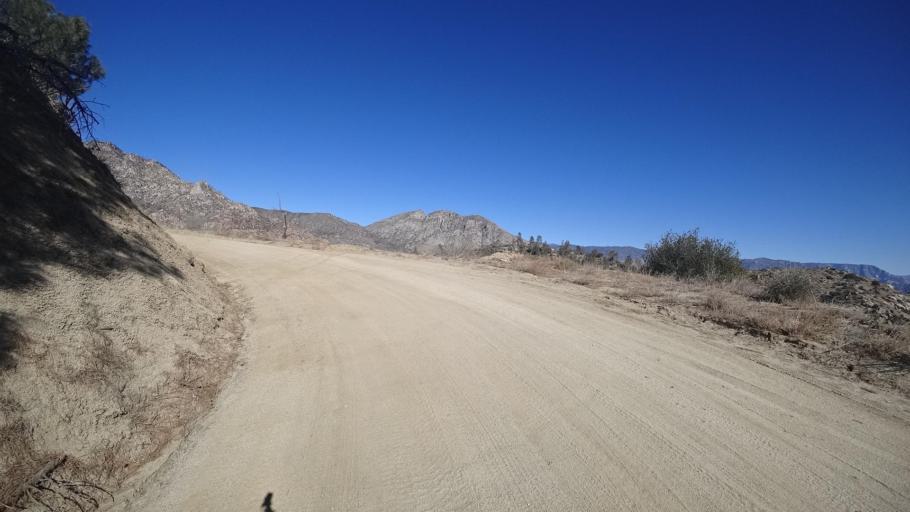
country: US
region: California
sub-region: Kern County
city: Wofford Heights
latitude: 35.7057
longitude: -118.4995
